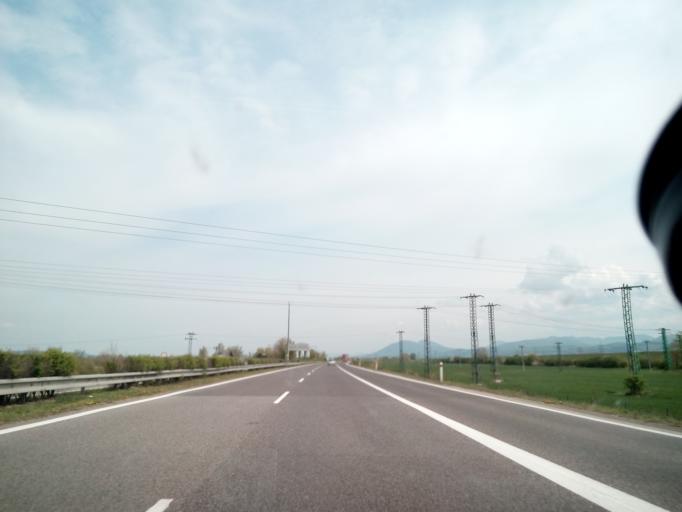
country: SK
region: Nitriansky
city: Nemsova
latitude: 48.9643
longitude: 18.1413
